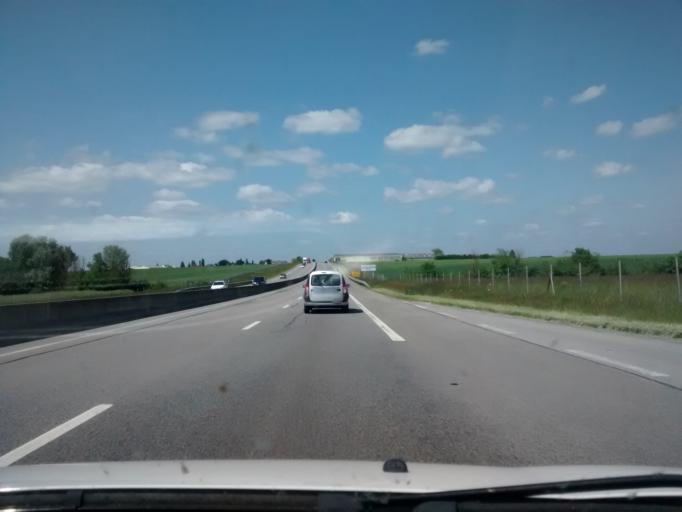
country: FR
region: Ile-de-France
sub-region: Departement des Yvelines
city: Ablis
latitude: 48.5577
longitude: 1.8314
